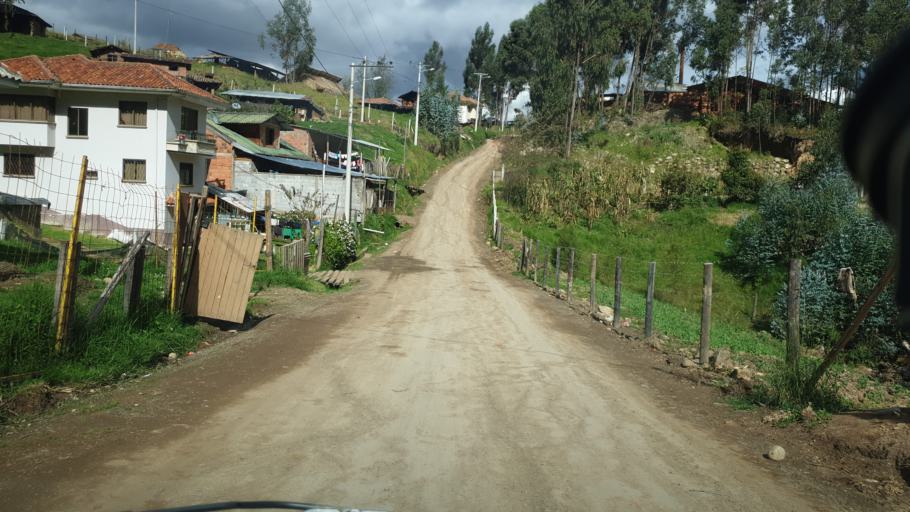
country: EC
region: Azuay
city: Cuenca
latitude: -2.8587
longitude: -79.0421
